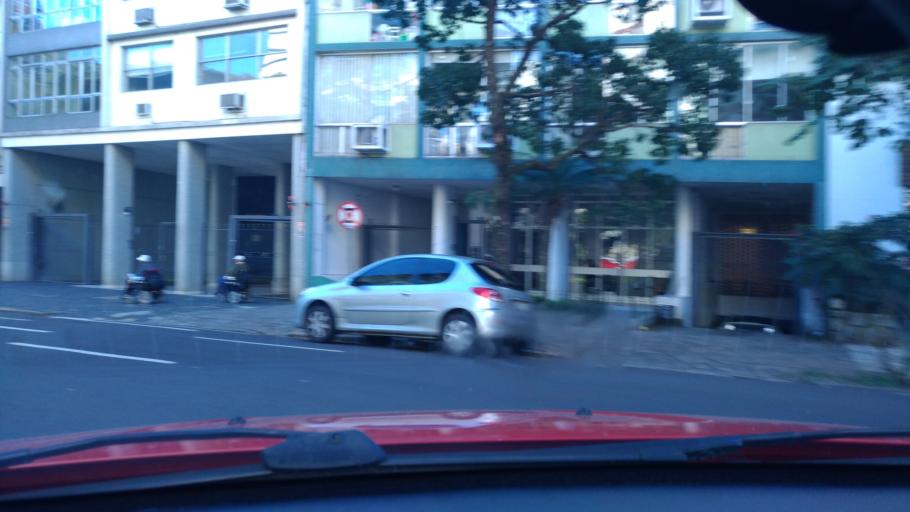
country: BR
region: Rio Grande do Sul
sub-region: Porto Alegre
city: Porto Alegre
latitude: -30.0285
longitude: -51.2076
